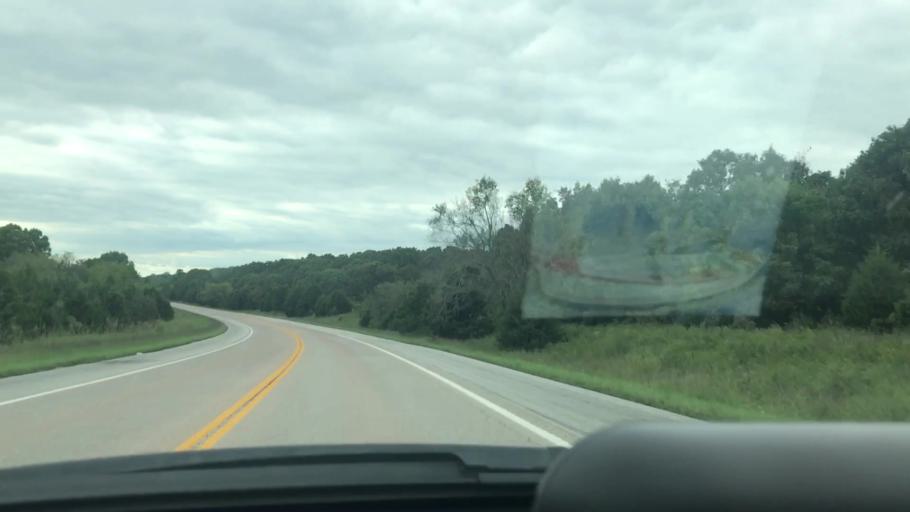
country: US
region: Missouri
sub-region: Benton County
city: Warsaw
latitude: 38.2078
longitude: -93.3299
